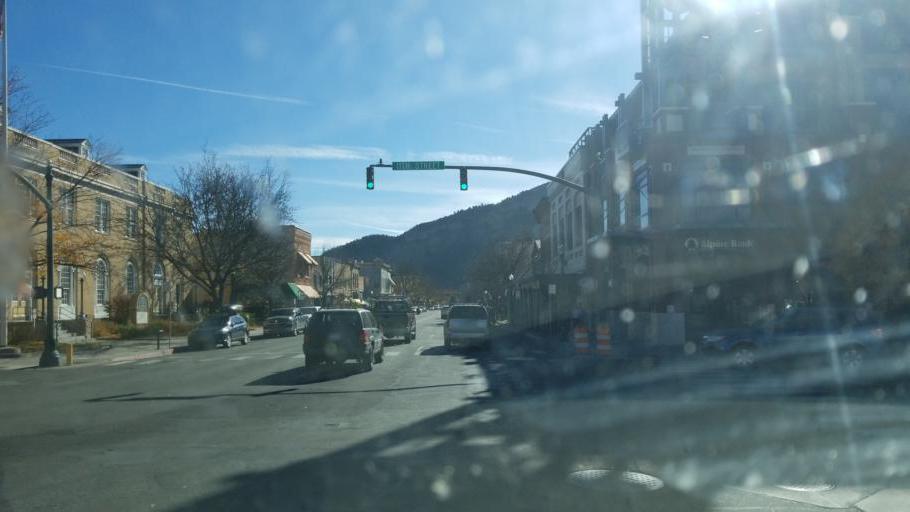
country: US
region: Colorado
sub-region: La Plata County
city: Durango
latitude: 37.2757
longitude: -107.8801
